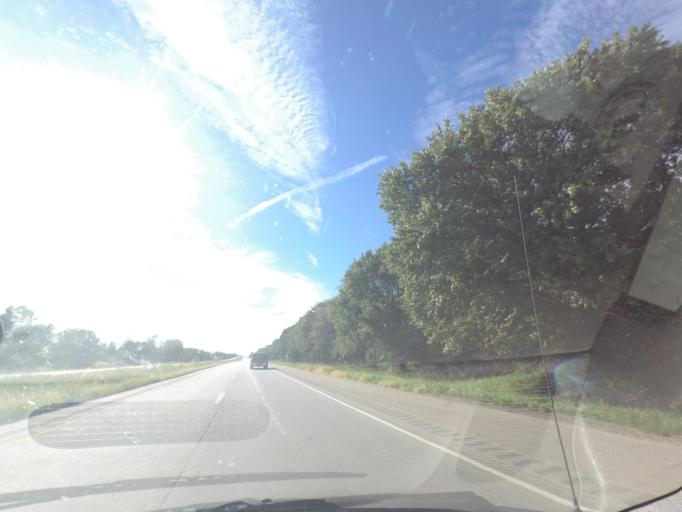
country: US
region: Illinois
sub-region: Macon County
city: Forsyth
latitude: 39.9096
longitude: -88.9177
